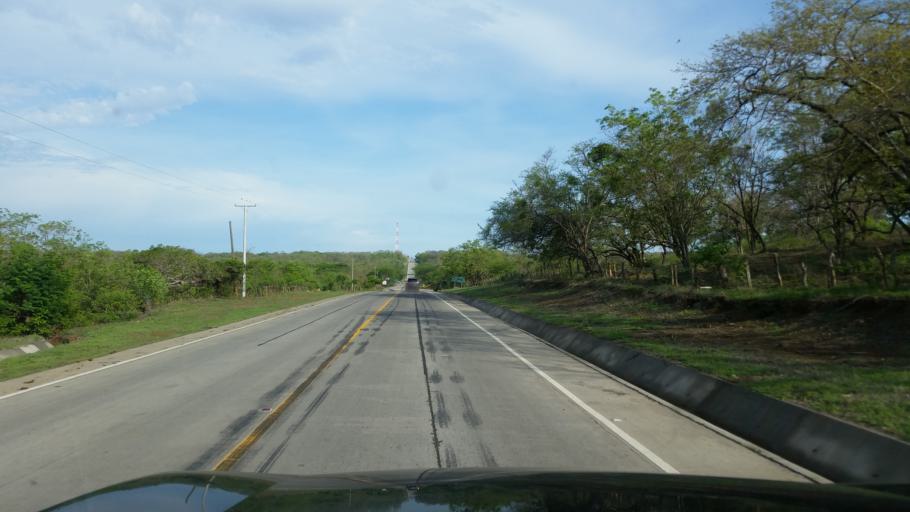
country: NI
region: Leon
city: Nagarote
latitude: 12.1151
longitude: -86.6114
